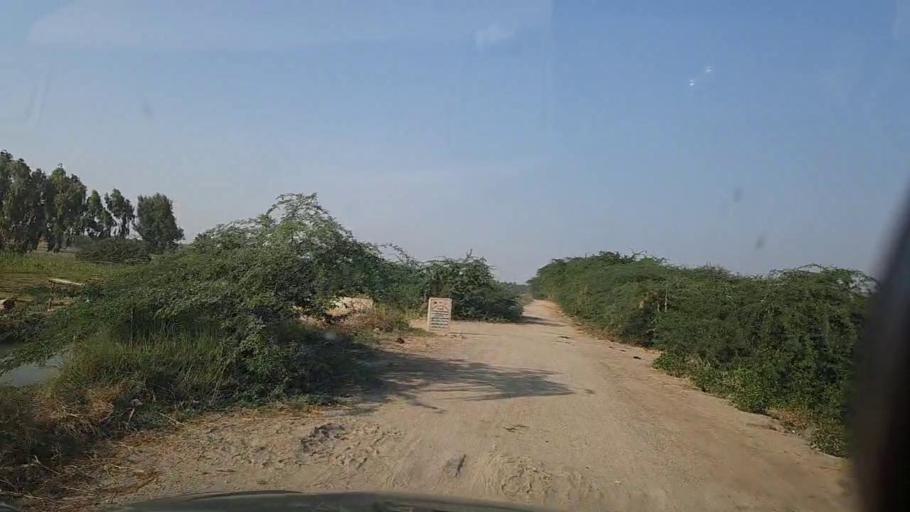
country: PK
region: Sindh
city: Thatta
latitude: 24.6175
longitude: 67.8762
